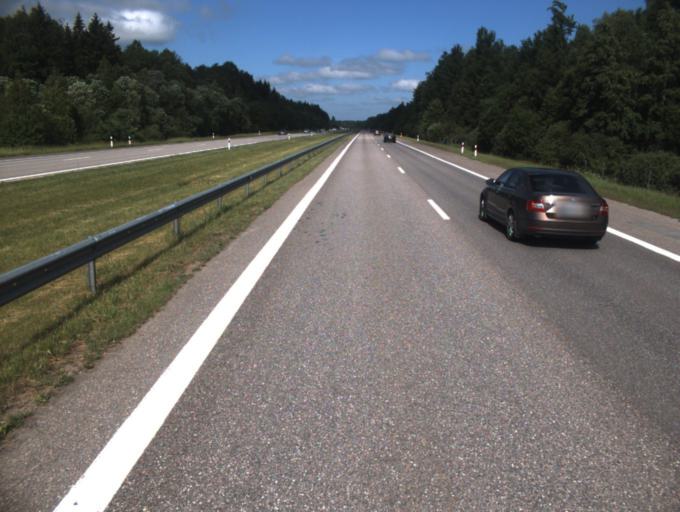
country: LT
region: Klaipedos apskritis
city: Gargzdai
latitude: 55.7011
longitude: 21.6188
